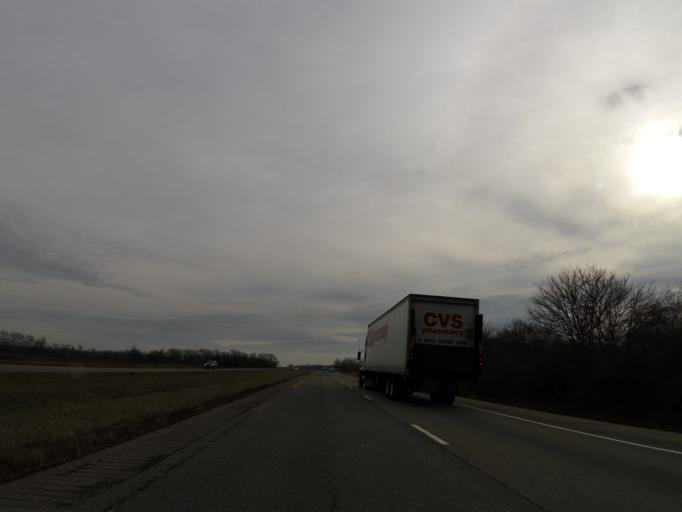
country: US
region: Indiana
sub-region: Montgomery County
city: Crawfordsville
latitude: 40.1026
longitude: -87.0617
